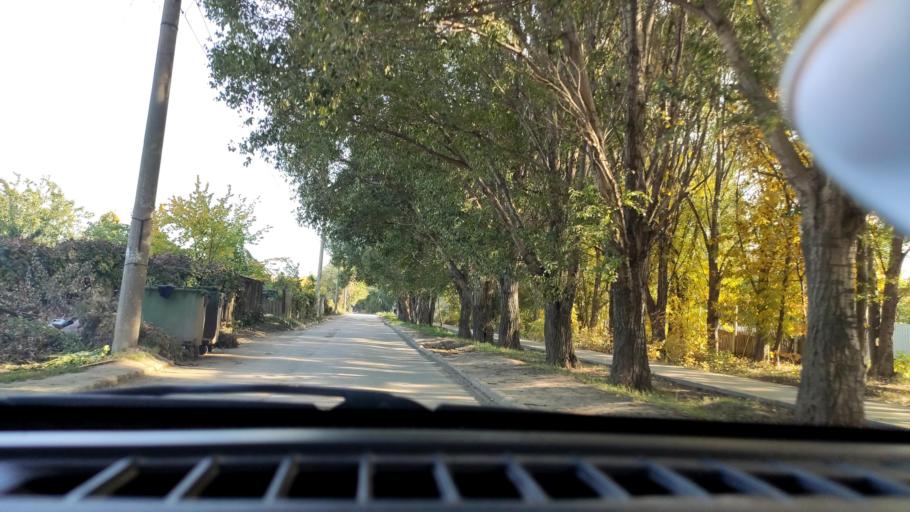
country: RU
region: Samara
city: Smyshlyayevka
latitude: 53.1896
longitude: 50.2818
